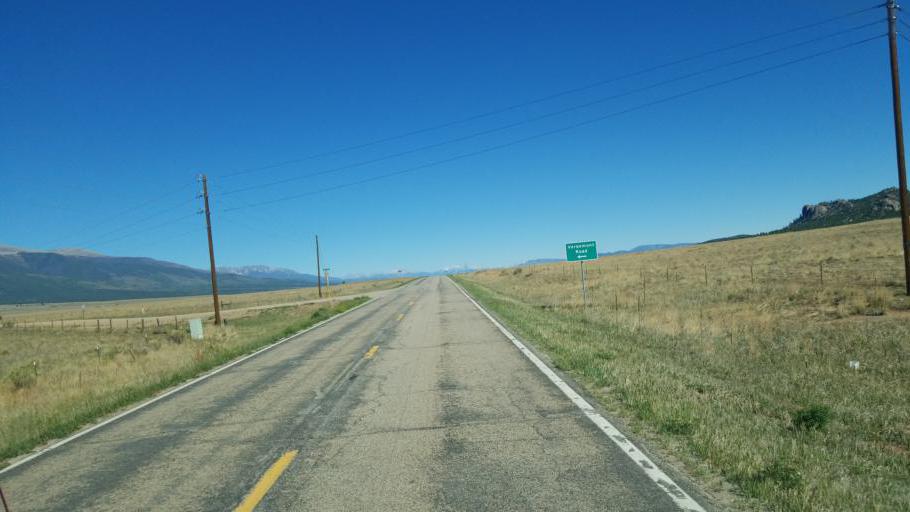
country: US
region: Colorado
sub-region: Custer County
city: Westcliffe
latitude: 38.1980
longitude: -105.5304
